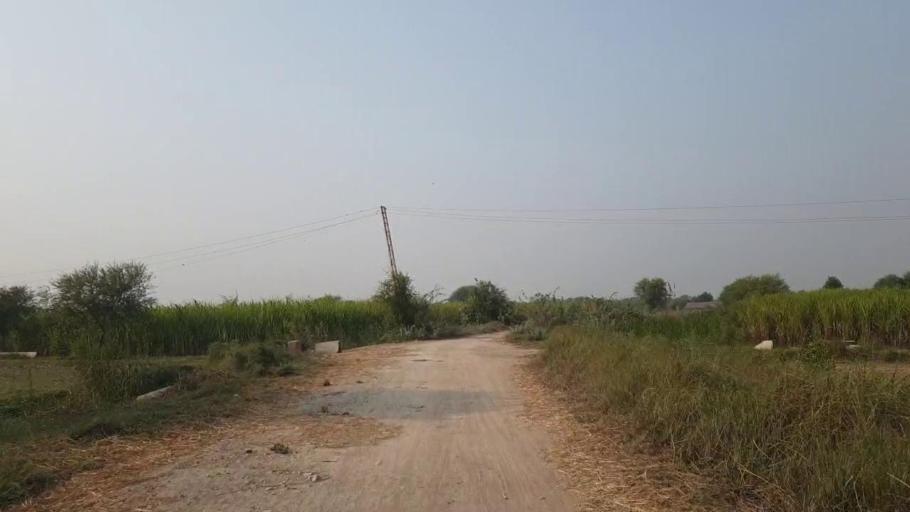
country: PK
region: Sindh
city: Tando Muhammad Khan
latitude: 25.1395
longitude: 68.6177
